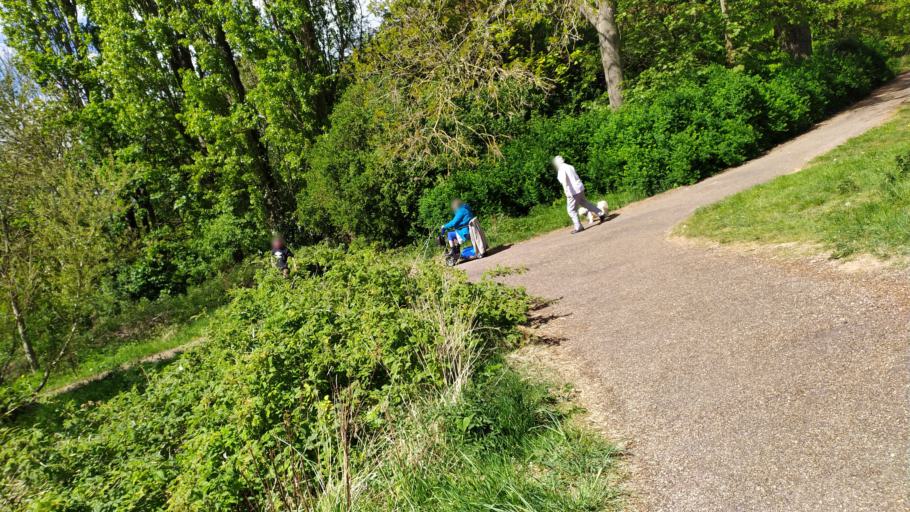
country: GB
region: England
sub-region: City and Borough of Leeds
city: Shadwell
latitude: 53.8081
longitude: -1.4841
